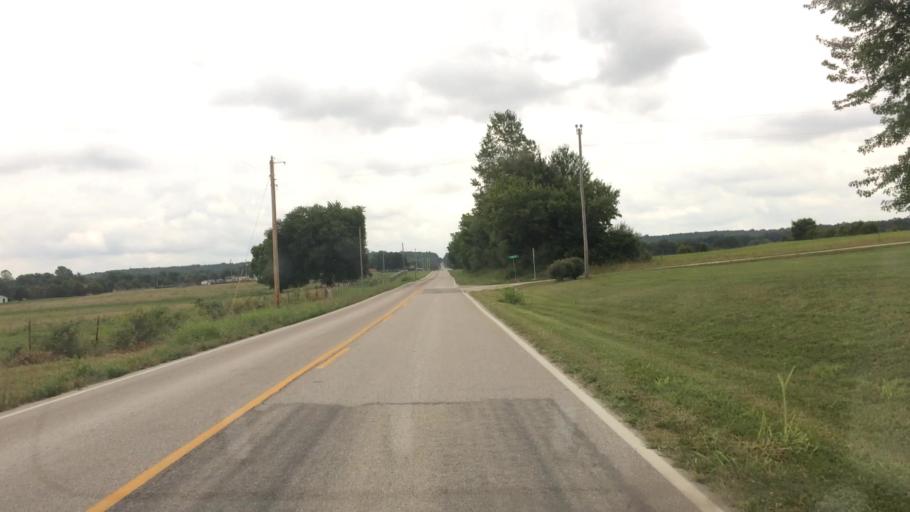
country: US
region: Missouri
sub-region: Webster County
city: Marshfield
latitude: 37.3412
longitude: -92.9999
